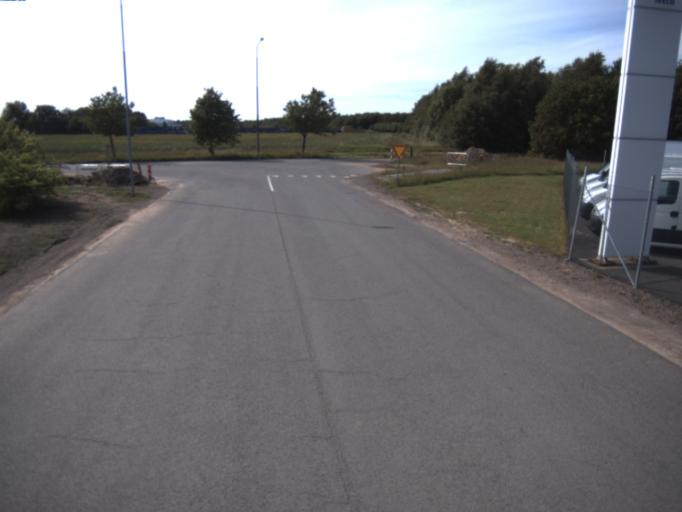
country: SE
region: Skane
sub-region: Helsingborg
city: Odakra
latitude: 56.0797
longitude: 12.7561
